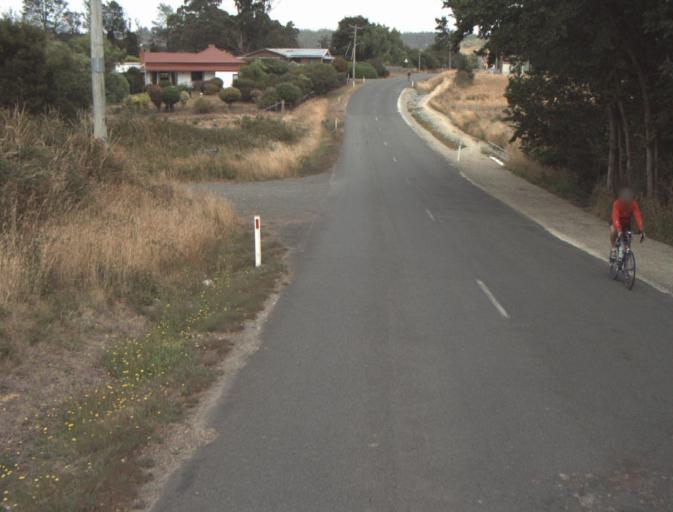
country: AU
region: Tasmania
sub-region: Launceston
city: Mayfield
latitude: -41.1759
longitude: 147.2291
